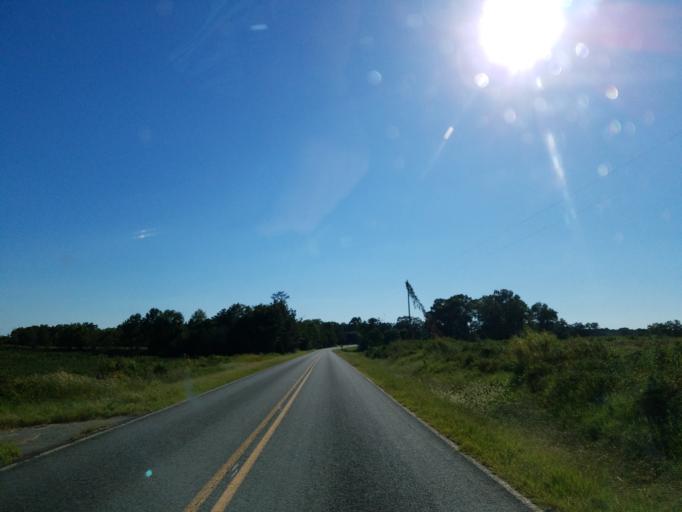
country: US
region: Georgia
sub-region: Dooly County
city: Unadilla
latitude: 32.2553
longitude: -83.7802
